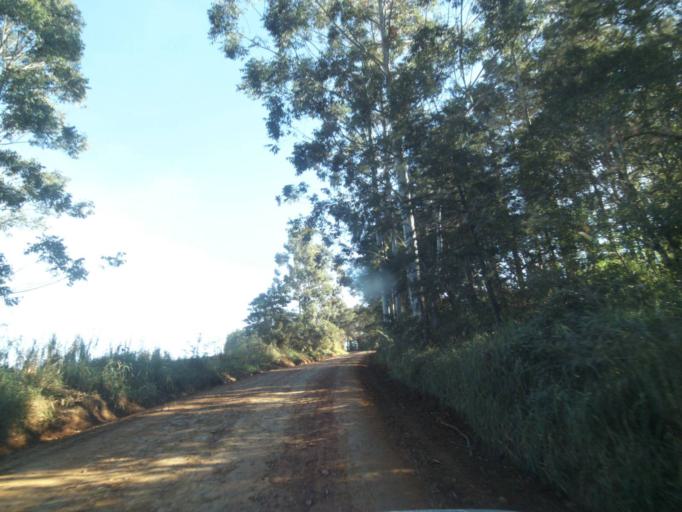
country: BR
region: Parana
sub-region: Tibagi
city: Tibagi
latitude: -24.5258
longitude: -50.5084
